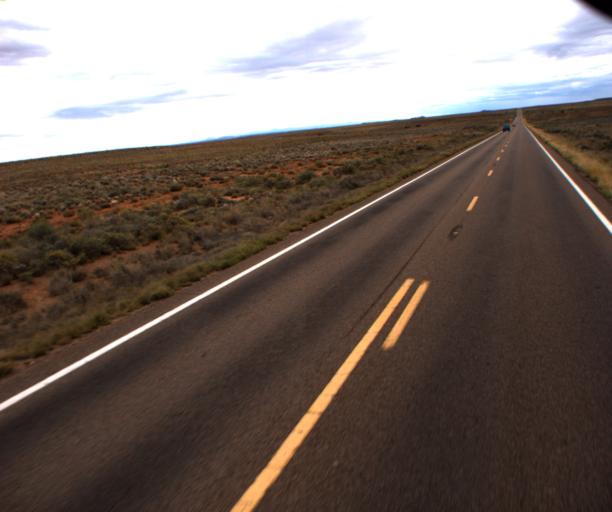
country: US
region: Arizona
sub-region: Navajo County
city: Holbrook
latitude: 34.7814
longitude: -110.1303
